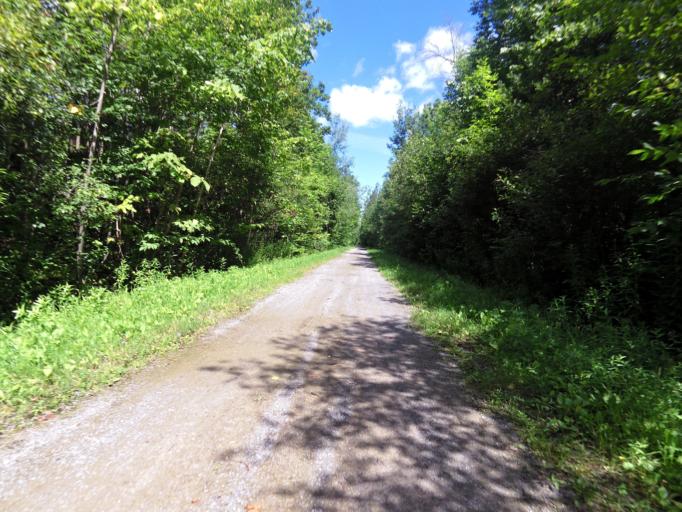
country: CA
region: Ontario
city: Ottawa
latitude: 45.2804
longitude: -75.6255
